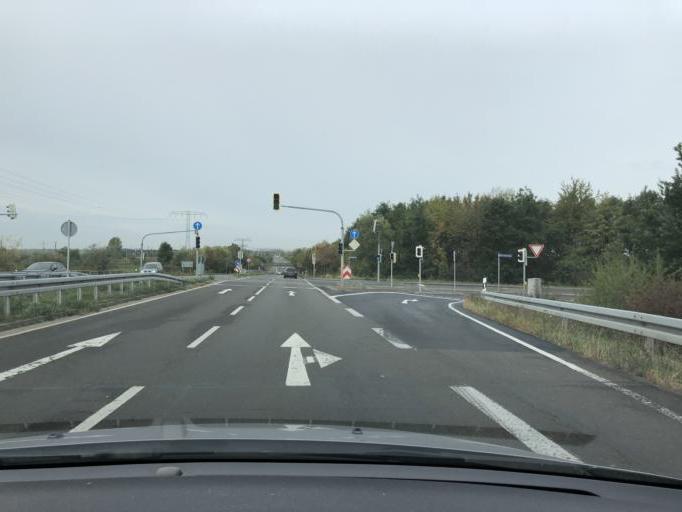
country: DE
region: Saxony
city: Schkeuditz
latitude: 51.3928
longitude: 12.2915
